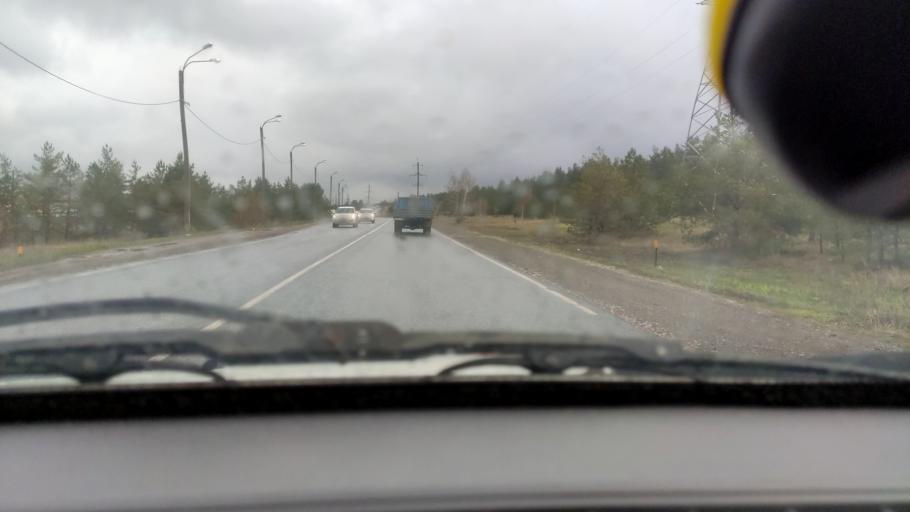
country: RU
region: Samara
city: Zhigulevsk
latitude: 53.5626
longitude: 49.5432
